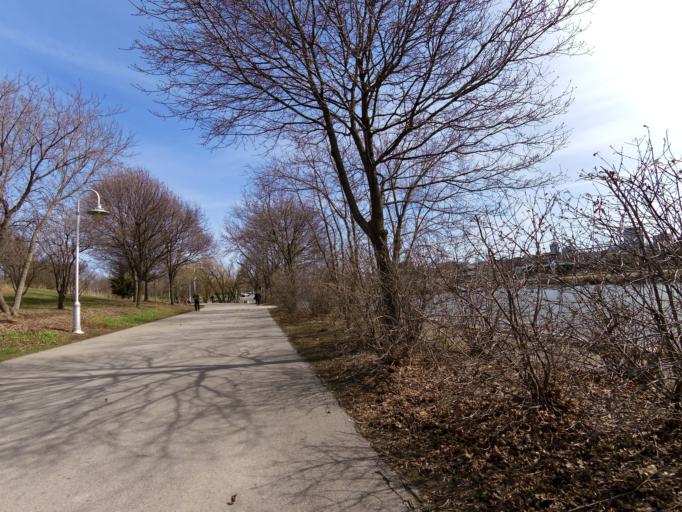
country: CA
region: Ontario
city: Hamilton
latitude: 43.2702
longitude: -79.8731
